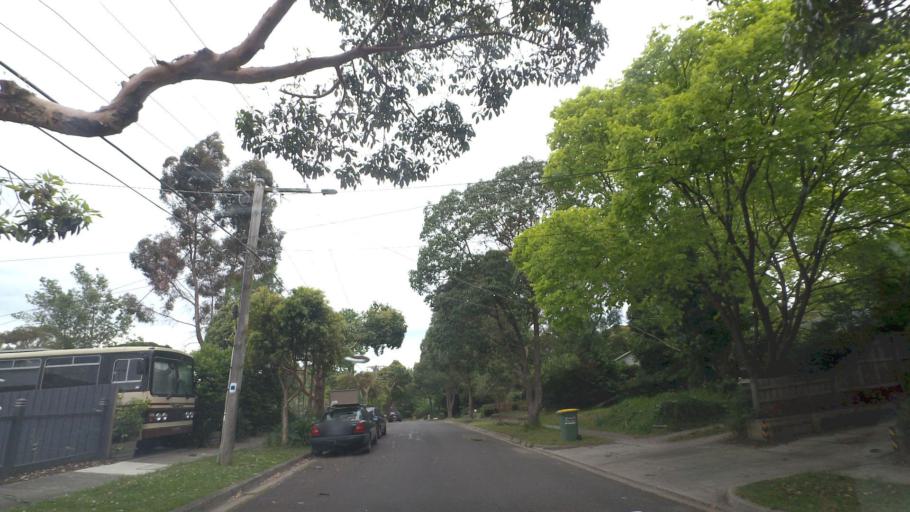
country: AU
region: Victoria
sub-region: Maroondah
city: Croydon North
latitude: -37.7924
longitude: 145.2989
